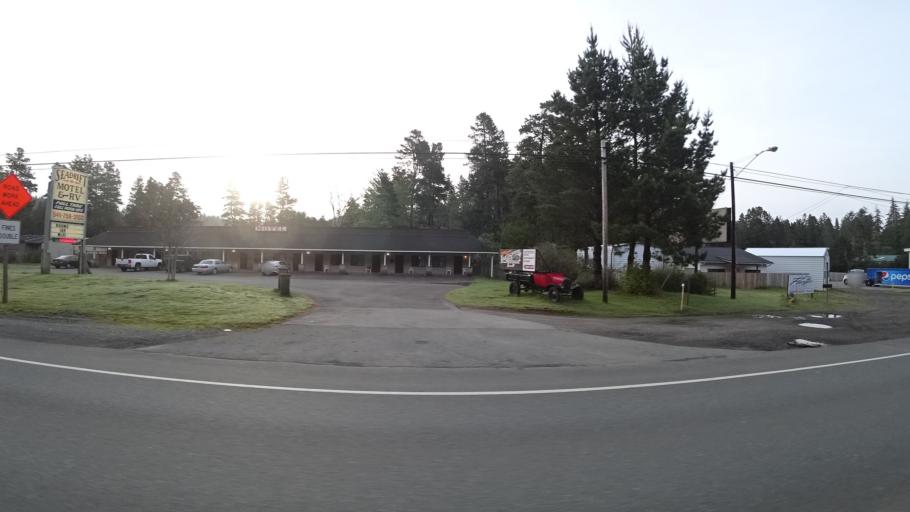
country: US
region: Oregon
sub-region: Coos County
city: Lakeside
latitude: 43.5956
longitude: -124.1814
